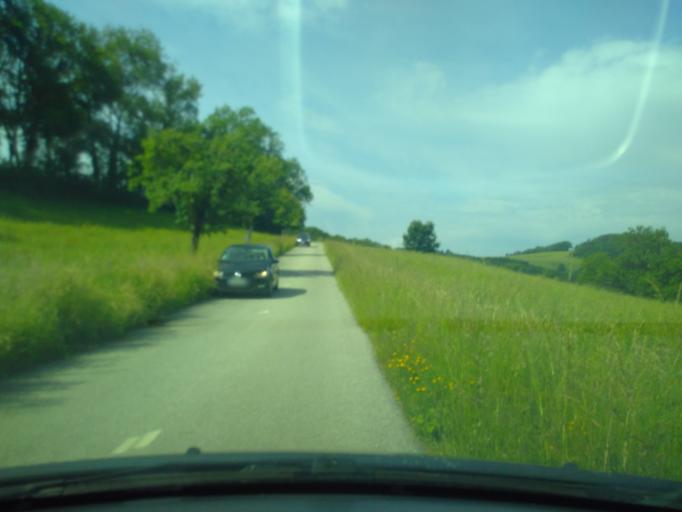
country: FR
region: Rhone-Alpes
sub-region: Departement de la Haute-Savoie
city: Beaumont
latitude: 46.0816
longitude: 6.1021
